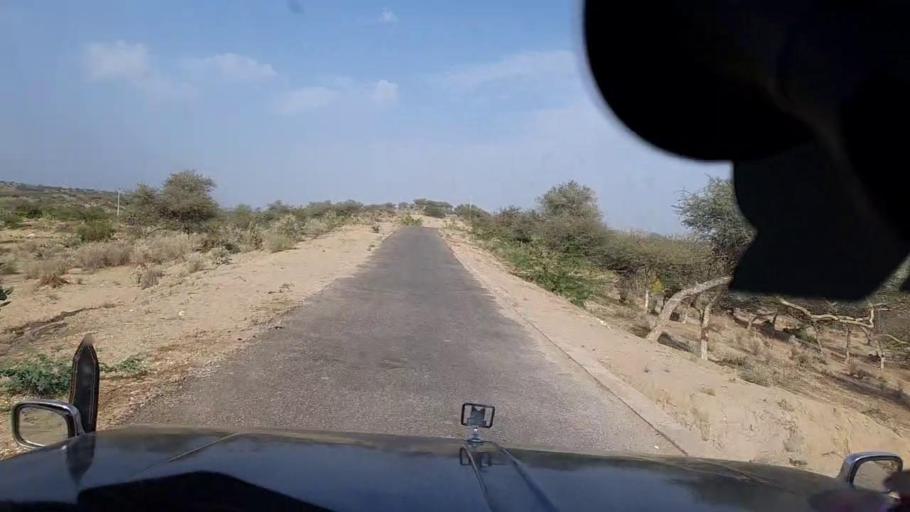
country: PK
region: Sindh
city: Diplo
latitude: 24.4887
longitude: 69.5431
